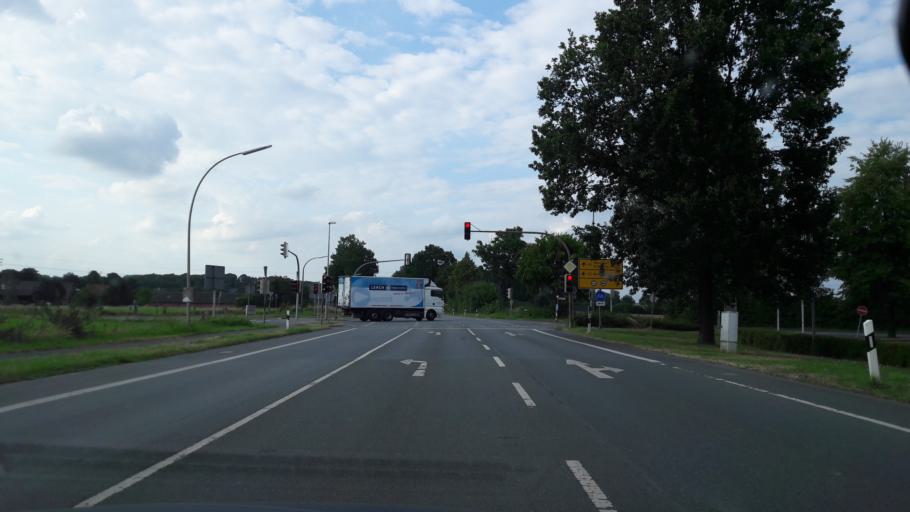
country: DE
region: North Rhine-Westphalia
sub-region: Regierungsbezirk Munster
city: Ennigerloh
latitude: 51.8059
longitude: 8.0258
